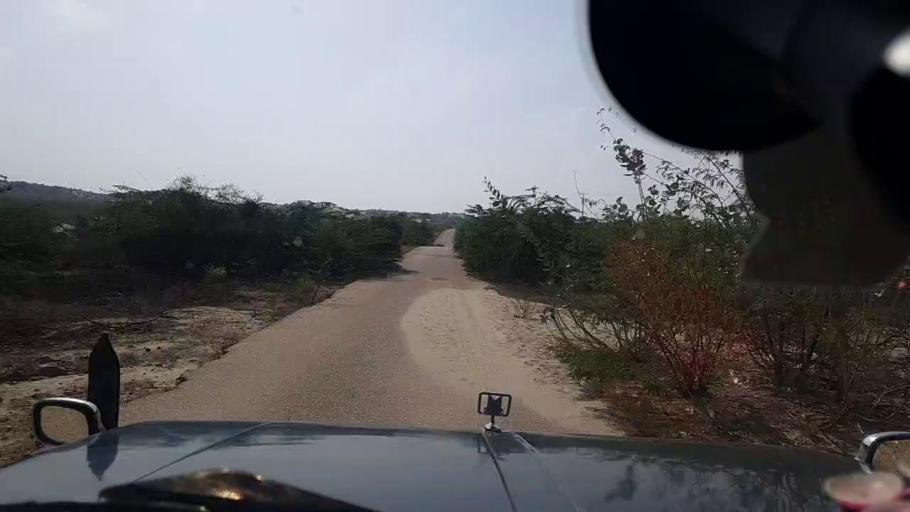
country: PK
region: Sindh
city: Diplo
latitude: 24.4183
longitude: 69.4649
